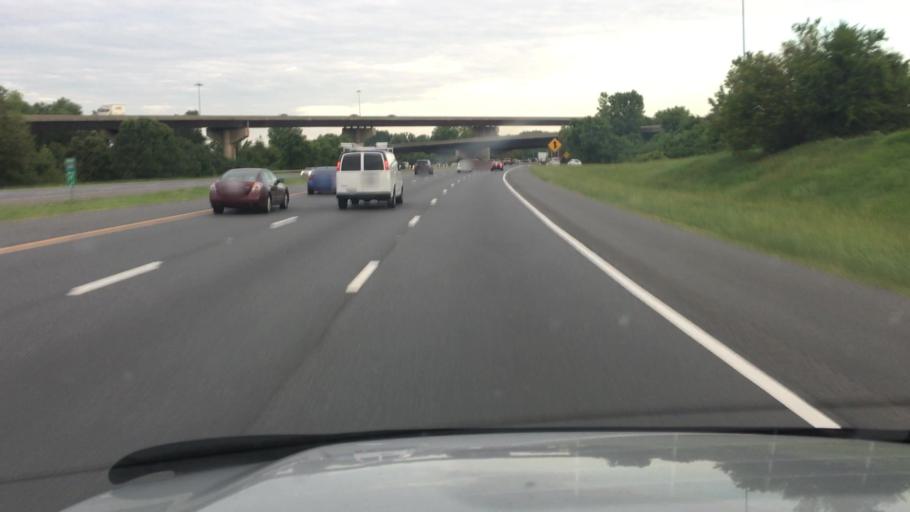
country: US
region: North Carolina
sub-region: Mecklenburg County
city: Pineville
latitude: 35.1241
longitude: -80.9144
